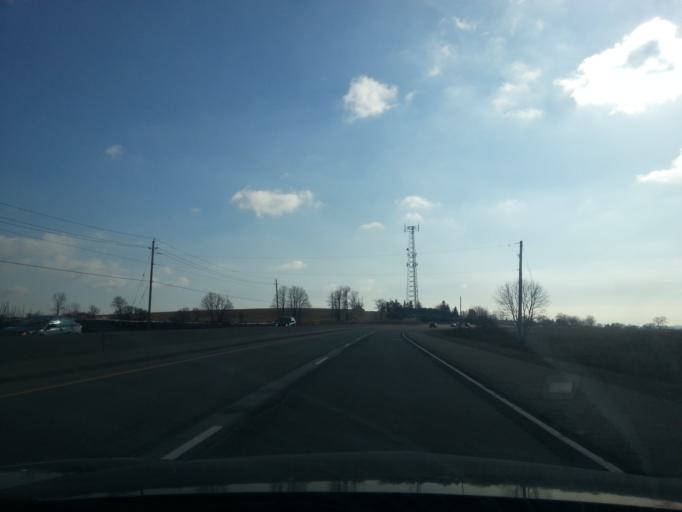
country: CA
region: Ontario
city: Oshawa
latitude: 44.0033
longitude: -78.6055
